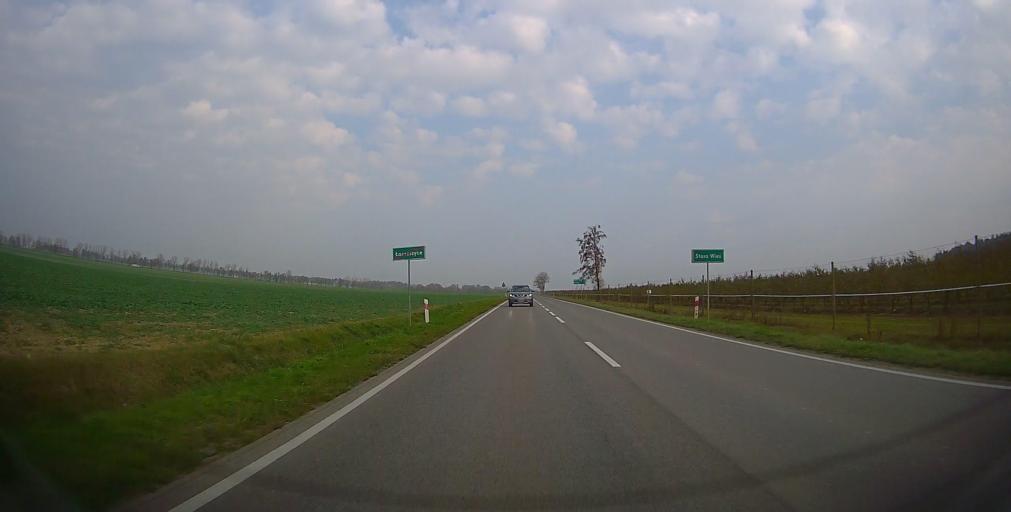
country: PL
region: Masovian Voivodeship
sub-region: Powiat grojecki
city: Belsk Duzy
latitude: 51.7992
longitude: 20.7882
